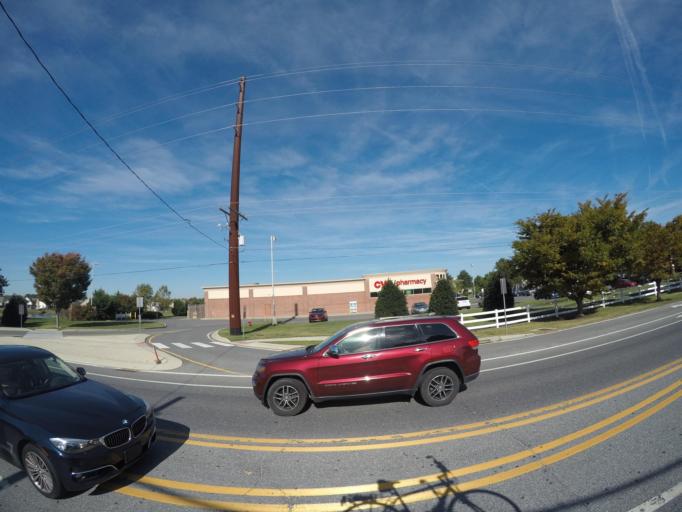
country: US
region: Delaware
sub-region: Sussex County
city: Lewes
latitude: 38.7502
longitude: -75.1686
